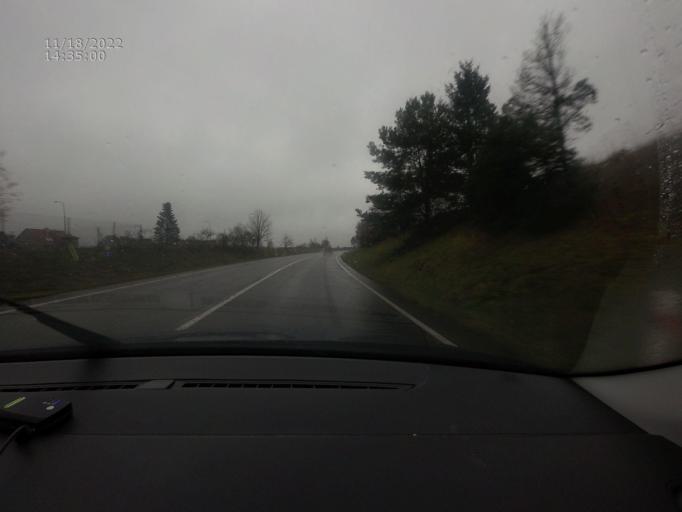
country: CZ
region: Jihocesky
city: Milevsko
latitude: 49.4561
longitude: 14.3331
